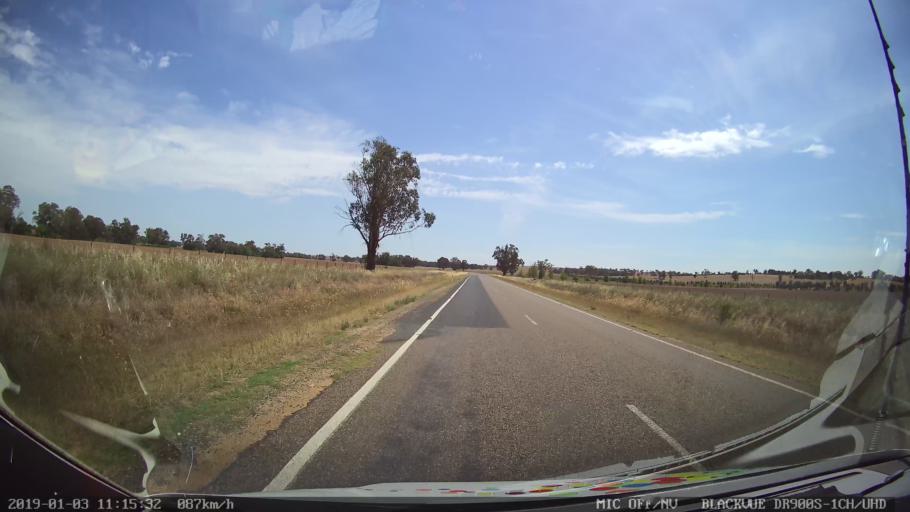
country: AU
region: New South Wales
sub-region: Young
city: Young
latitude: -34.1628
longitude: 148.2655
